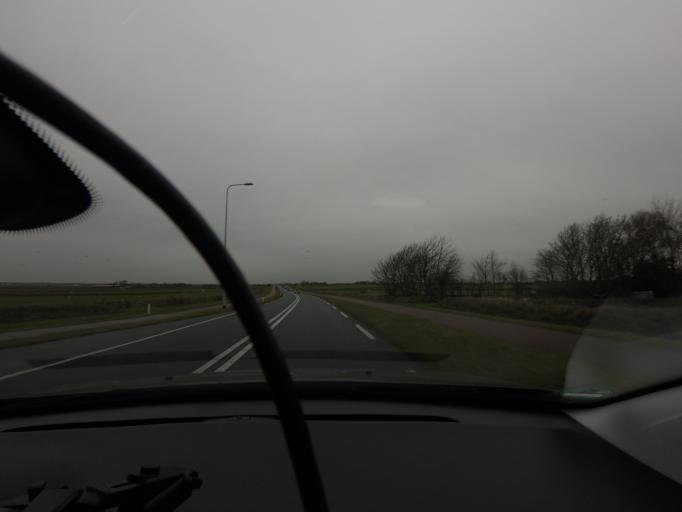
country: NL
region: North Holland
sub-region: Gemeente Texel
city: Den Burg
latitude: 53.0391
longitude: 4.8042
